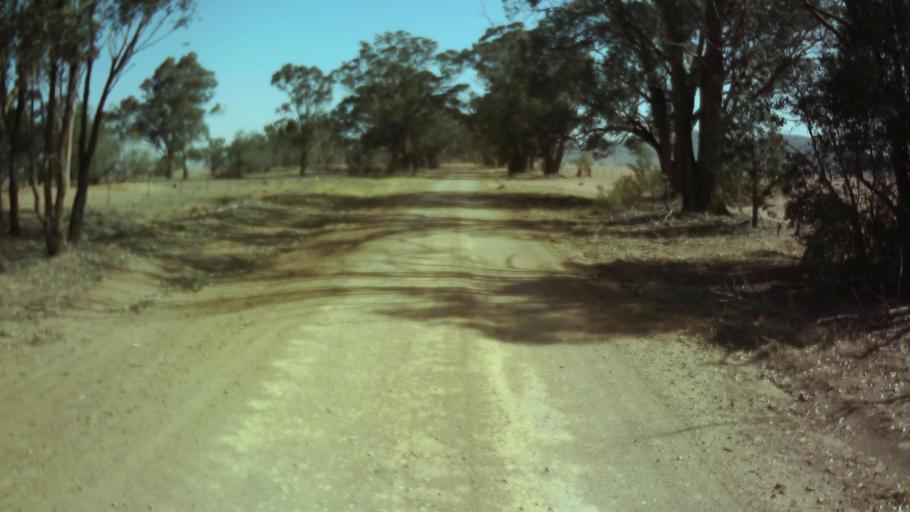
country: AU
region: New South Wales
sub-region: Weddin
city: Grenfell
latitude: -33.8453
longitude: 148.0173
